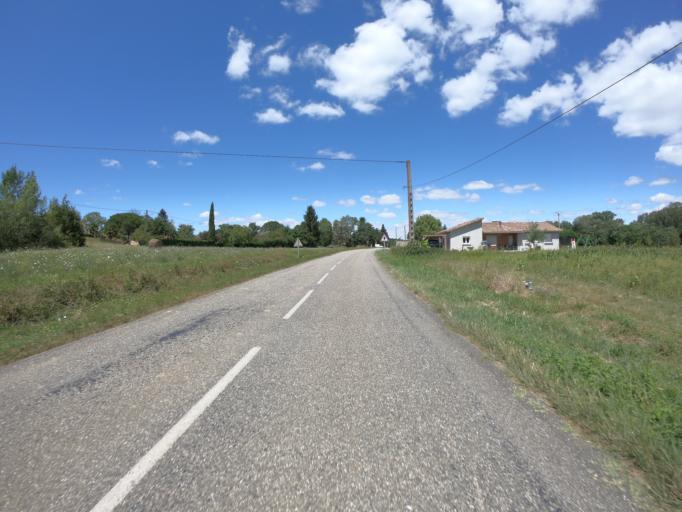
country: FR
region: Midi-Pyrenees
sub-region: Departement de l'Ariege
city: Verniolle
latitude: 43.0646
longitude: 1.7385
